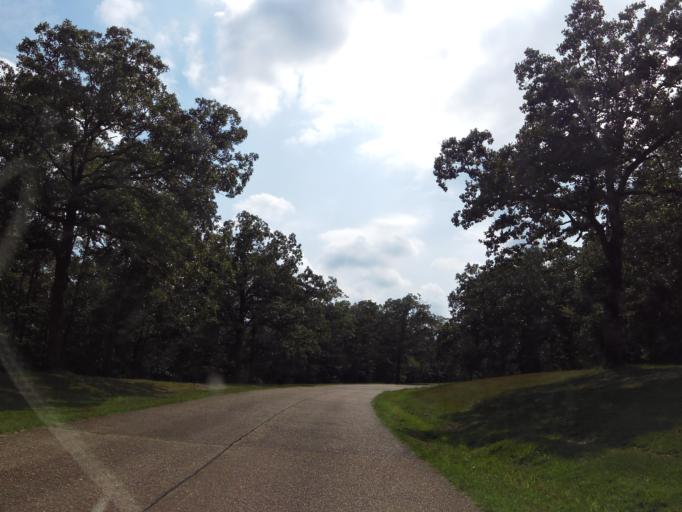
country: US
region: Tennessee
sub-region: Hardin County
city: Crump
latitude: 35.1488
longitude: -88.3289
